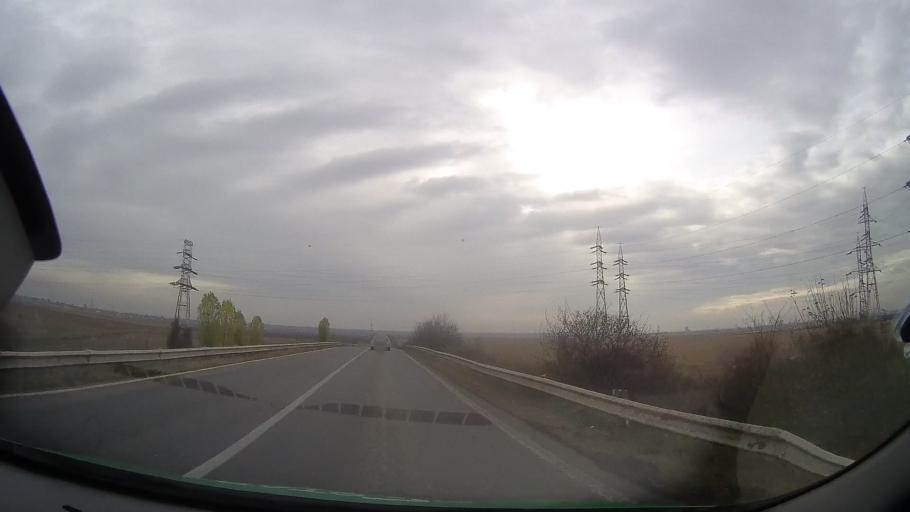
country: RO
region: Prahova
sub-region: Comuna Berceni
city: Berceni
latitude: 44.9406
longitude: 26.1018
